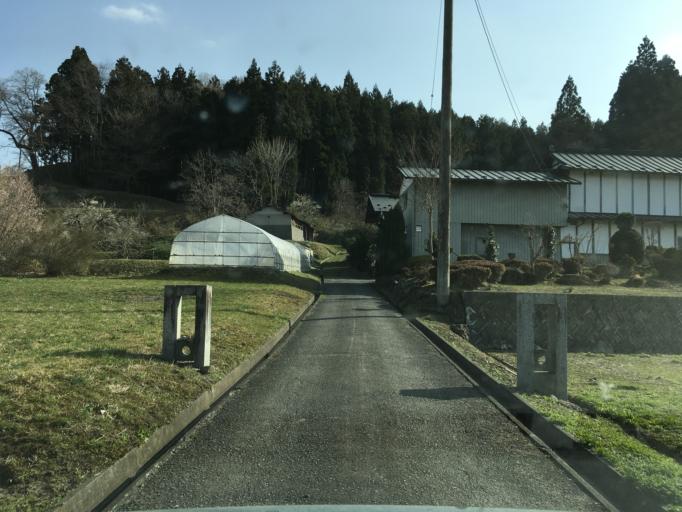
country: JP
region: Iwate
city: Ichinoseki
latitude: 38.9151
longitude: 141.0953
